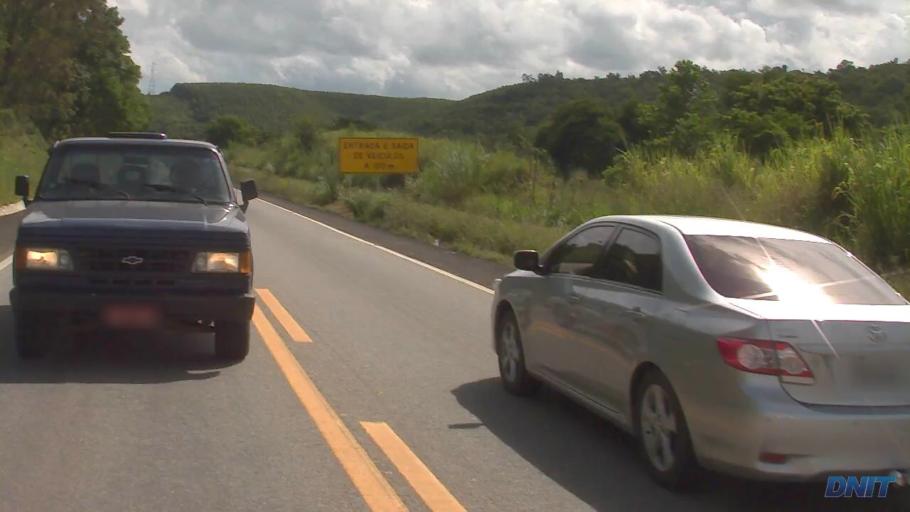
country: BR
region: Minas Gerais
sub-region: Ipaba
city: Ipaba
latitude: -19.3954
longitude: -42.4841
